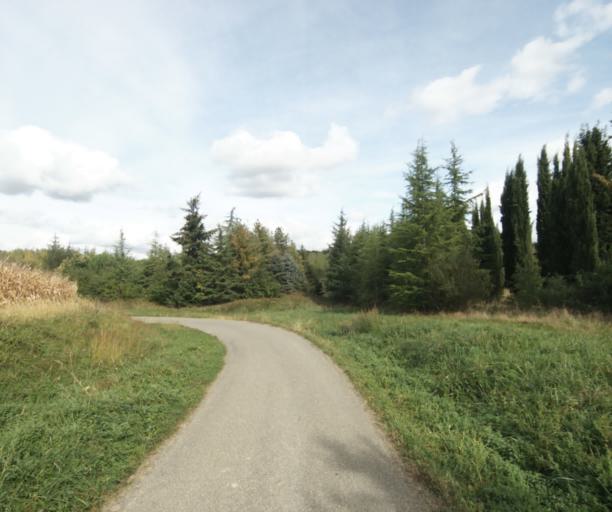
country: FR
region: Midi-Pyrenees
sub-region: Departement du Gers
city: Eauze
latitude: 43.8194
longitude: 0.1496
